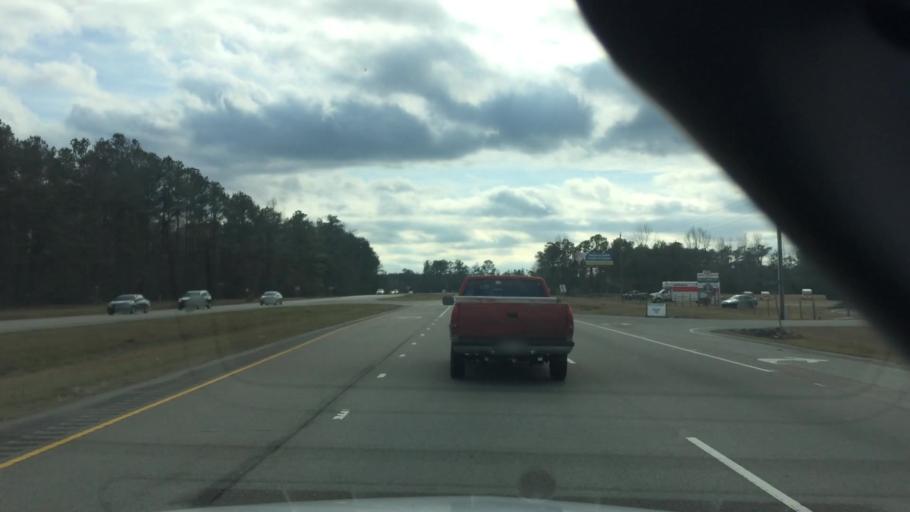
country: US
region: North Carolina
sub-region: Brunswick County
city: Bolivia
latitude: 34.1543
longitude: -78.0928
